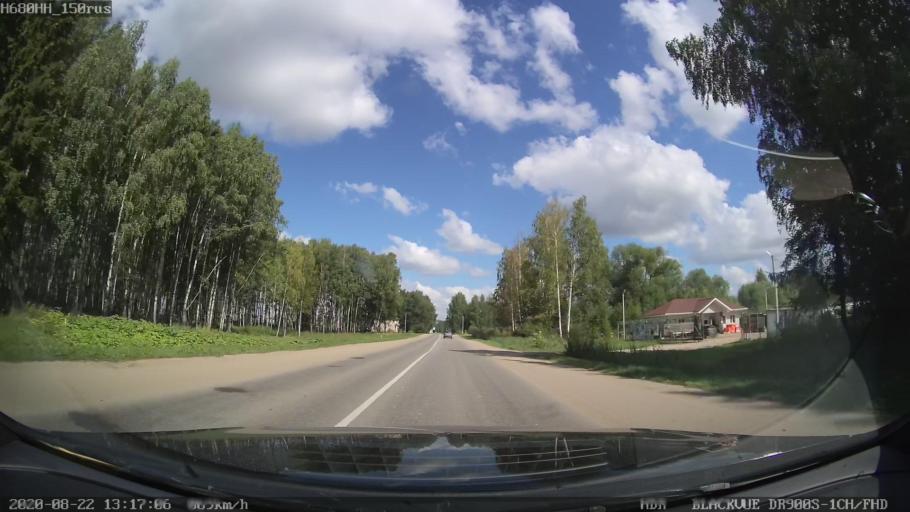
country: RU
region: Tverskaya
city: Bezhetsk
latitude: 57.7700
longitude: 36.6670
